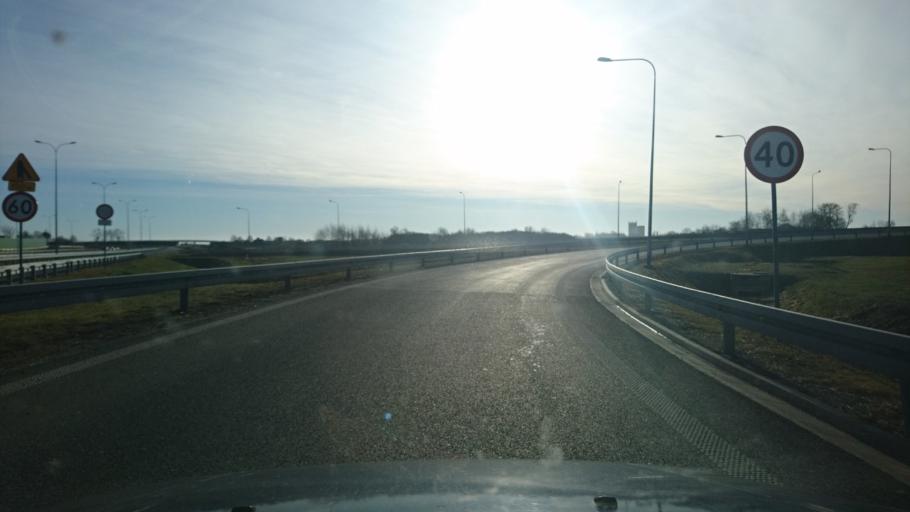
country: PL
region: Greater Poland Voivodeship
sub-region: Powiat kepinski
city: Kepno
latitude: 51.3149
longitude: 18.0098
